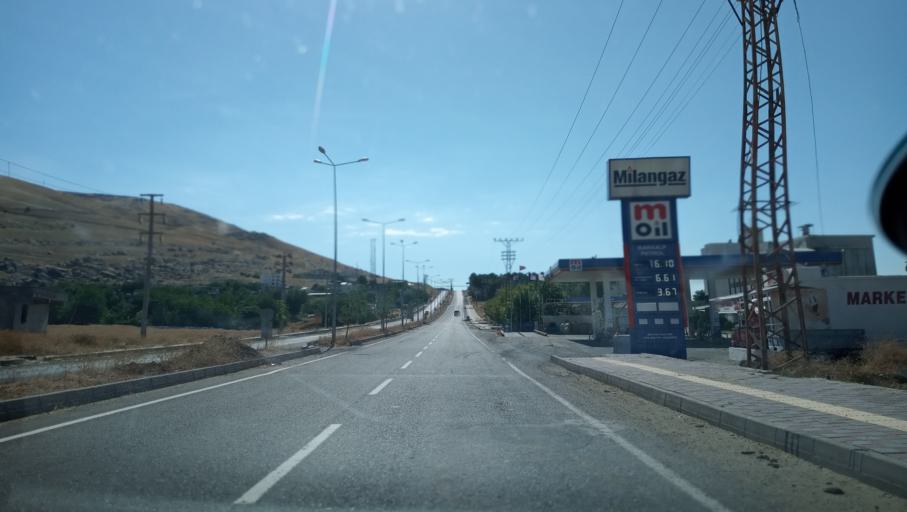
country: TR
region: Diyarbakir
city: Silvan
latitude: 38.1348
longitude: 41.0332
